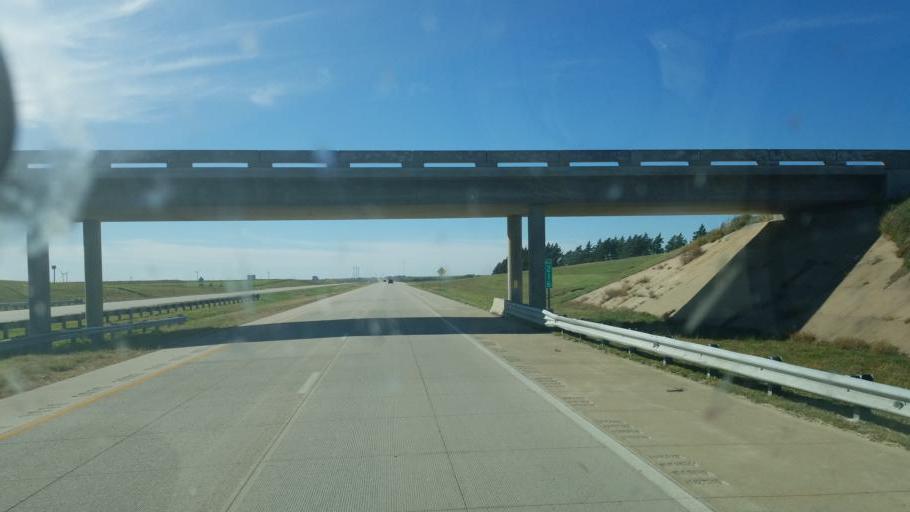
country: US
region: Kansas
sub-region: Ellsworth County
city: Ellsworth
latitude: 38.8494
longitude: -98.2807
